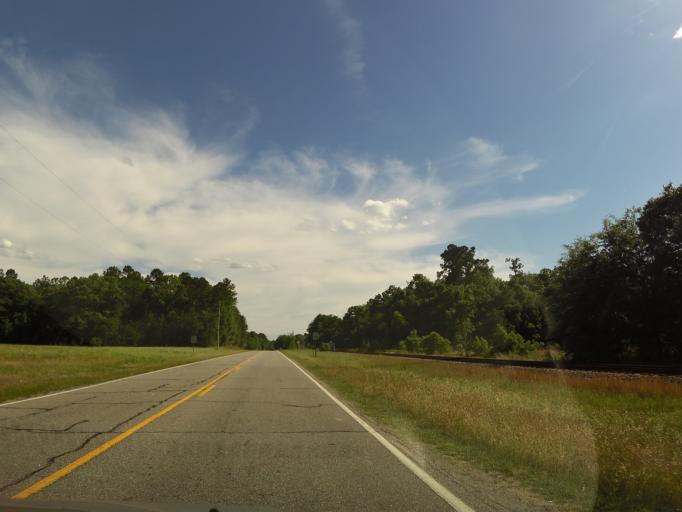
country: US
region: South Carolina
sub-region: Bamberg County
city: Denmark
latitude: 33.2190
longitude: -81.1750
